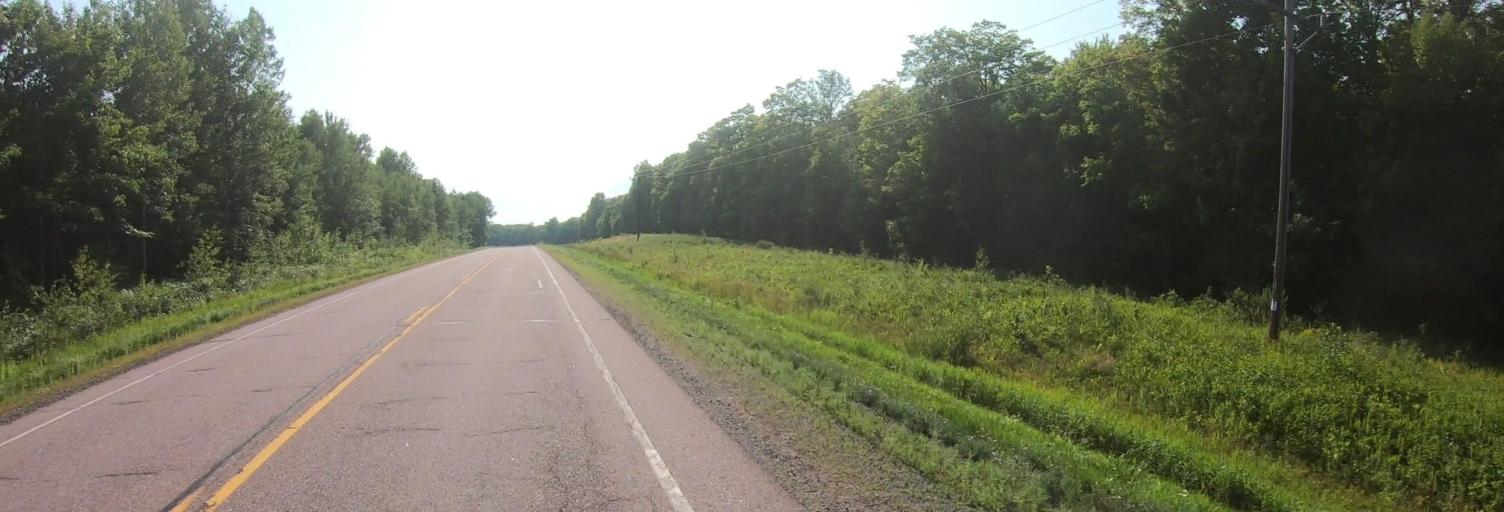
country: US
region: Wisconsin
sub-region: Iron County
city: Hurley
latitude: 46.3553
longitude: -90.4692
